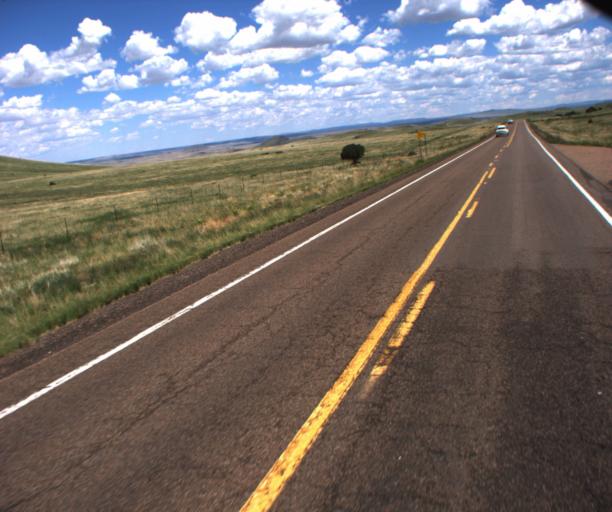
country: US
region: Arizona
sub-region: Apache County
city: Springerville
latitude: 34.2191
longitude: -109.4754
